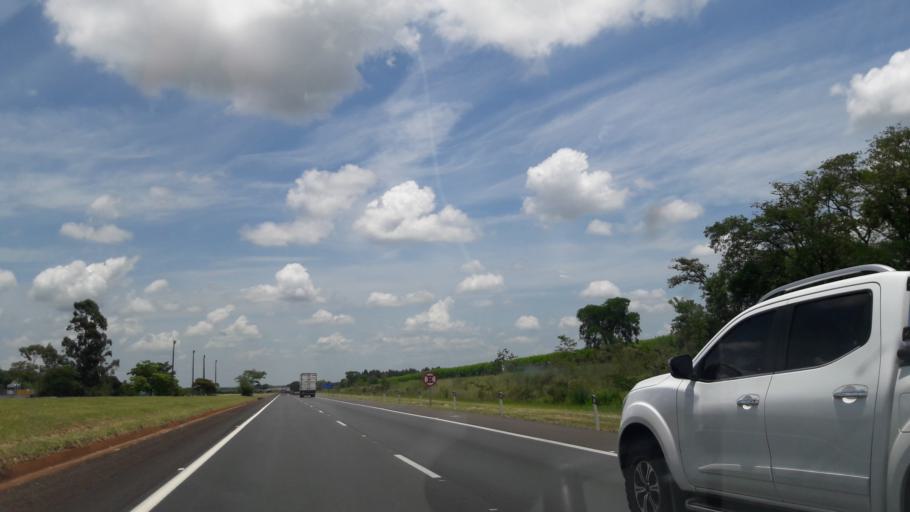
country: BR
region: Sao Paulo
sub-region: Avare
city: Avare
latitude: -22.9549
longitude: -48.8673
